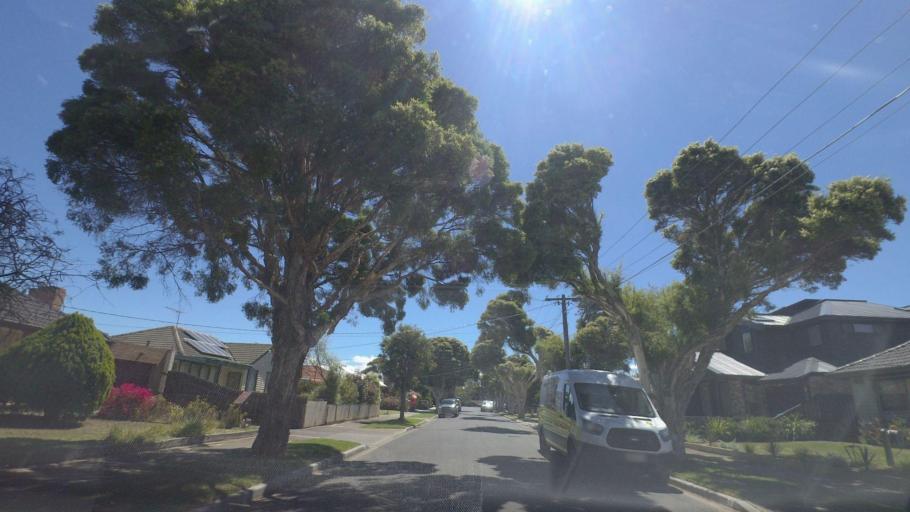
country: AU
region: Victoria
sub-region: Hobsons Bay
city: Altona
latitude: -37.8593
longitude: 144.8178
